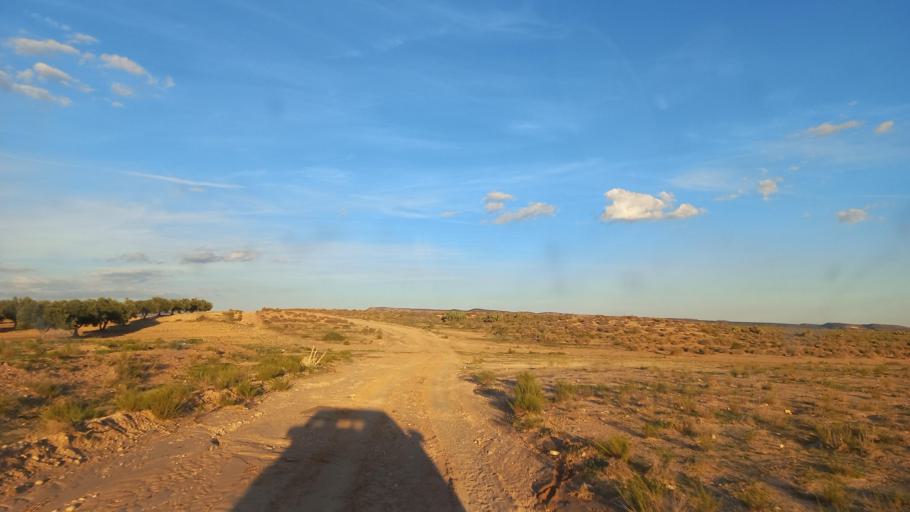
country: TN
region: Al Qasrayn
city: Sbiba
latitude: 35.3475
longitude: 9.0273
